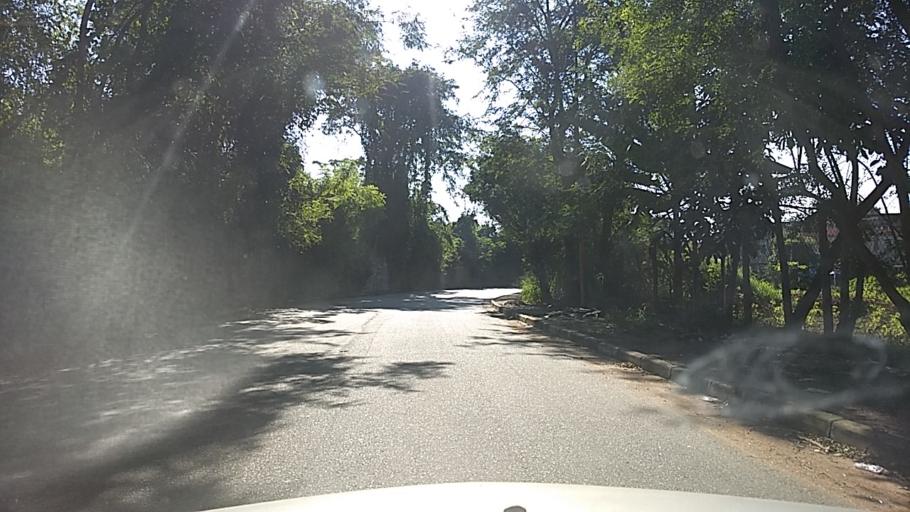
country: BR
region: Sao Paulo
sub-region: Osasco
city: Osasco
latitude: -23.5123
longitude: -46.7947
